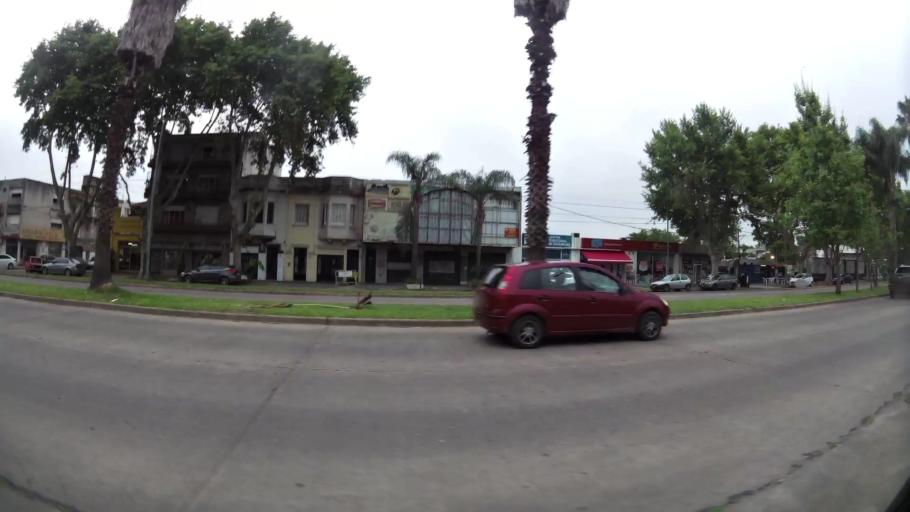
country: AR
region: Santa Fe
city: Granadero Baigorria
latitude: -32.9082
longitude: -60.6881
